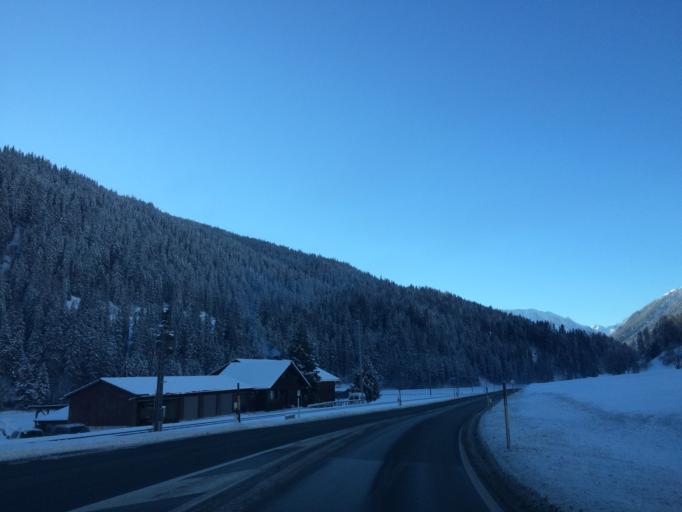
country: CH
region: Grisons
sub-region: Praettigau/Davos District
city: Davos
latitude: 46.7644
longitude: 9.7975
